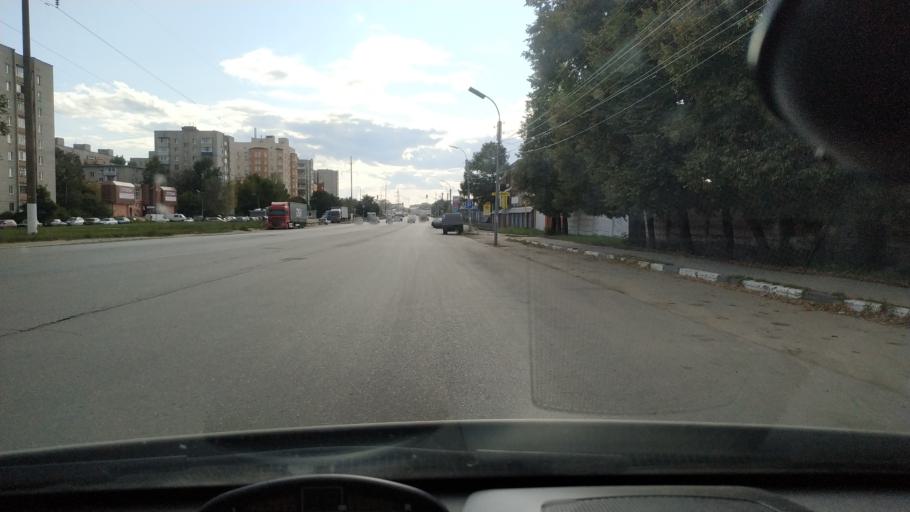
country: RU
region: Rjazan
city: Ryazan'
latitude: 54.6206
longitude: 39.7023
